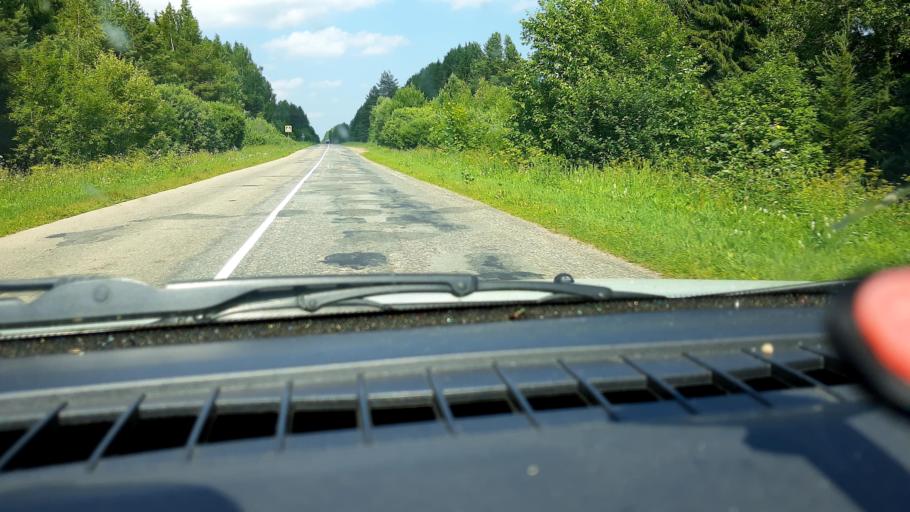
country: RU
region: Nizjnij Novgorod
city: Sharanga
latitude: 57.1033
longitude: 46.5300
